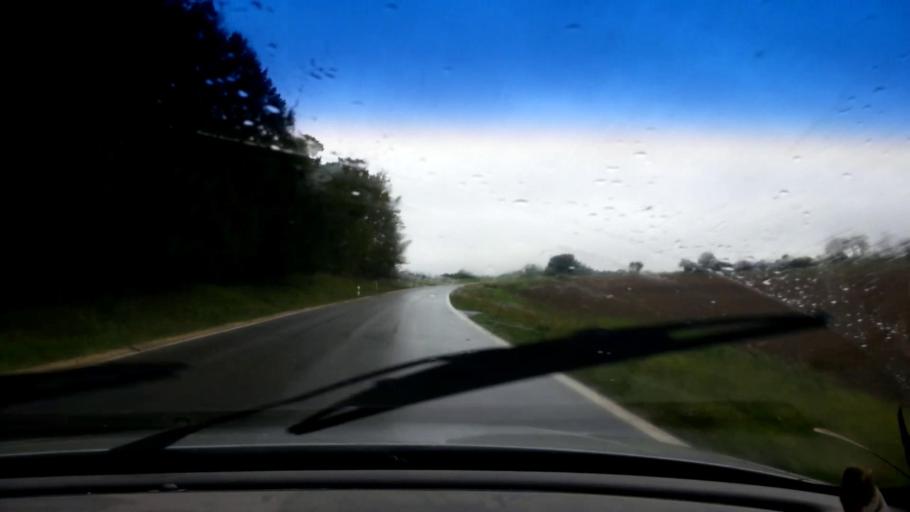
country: DE
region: Bavaria
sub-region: Upper Franconia
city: Poxdorf
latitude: 49.9378
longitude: 11.1331
